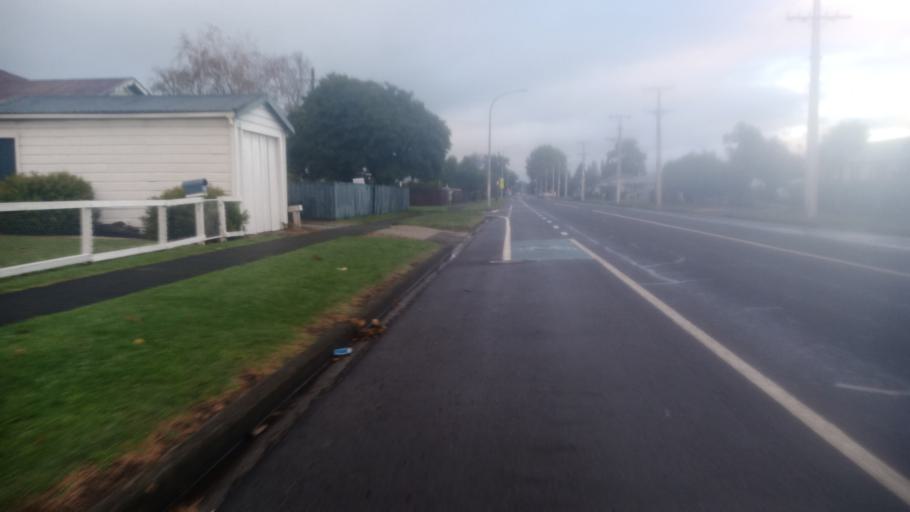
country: NZ
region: Gisborne
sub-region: Gisborne District
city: Gisborne
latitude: -38.6540
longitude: 177.9971
